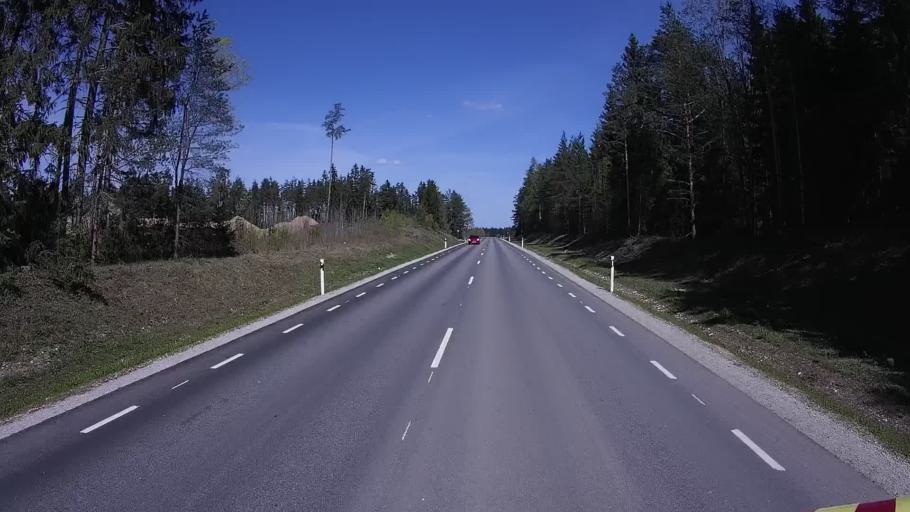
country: EE
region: Harju
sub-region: Paldiski linn
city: Paldiski
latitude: 59.1901
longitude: 24.0909
